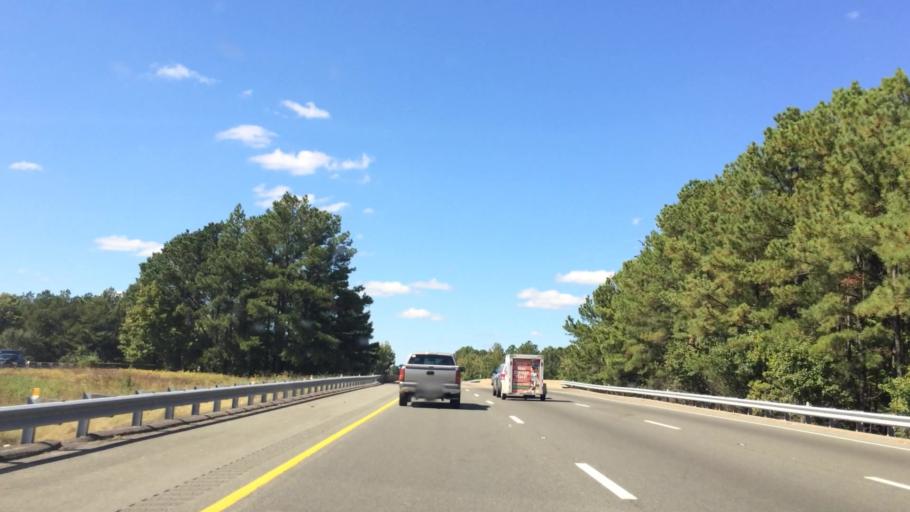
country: US
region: Virginia
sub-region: Henrico County
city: Glen Allen
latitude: 37.6765
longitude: -77.5017
